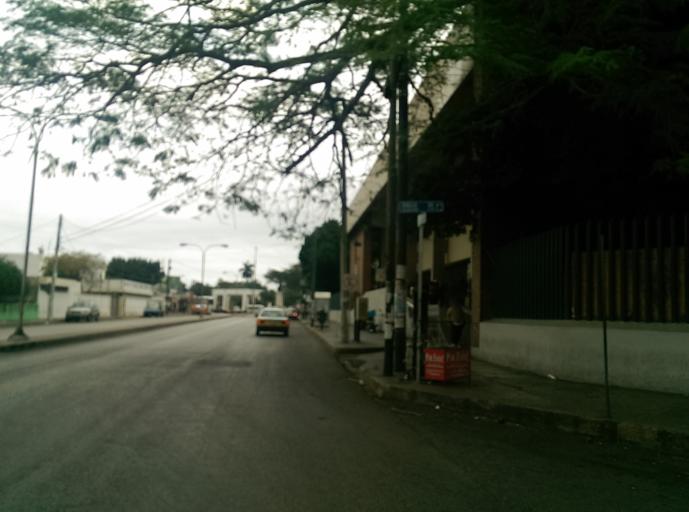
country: MX
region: Yucatan
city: Merida
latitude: 20.9889
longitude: -89.6405
